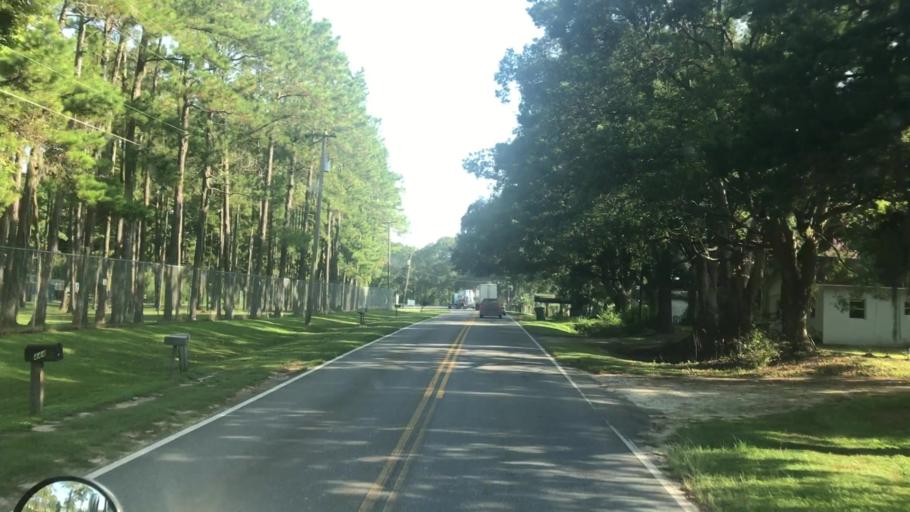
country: US
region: Florida
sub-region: Gadsden County
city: Quincy
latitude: 30.6045
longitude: -84.5723
